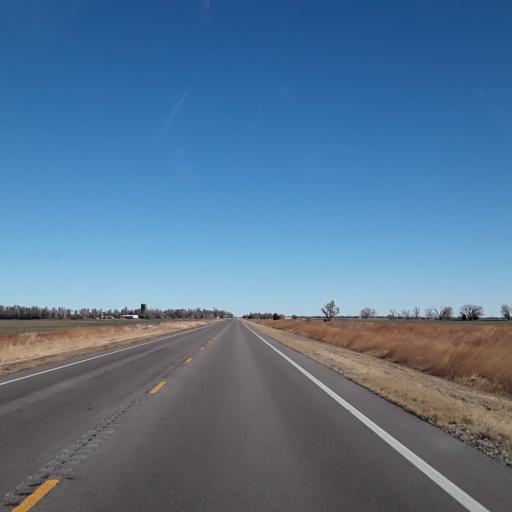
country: US
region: Kansas
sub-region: Pawnee County
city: Larned
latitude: 38.1100
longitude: -99.1936
